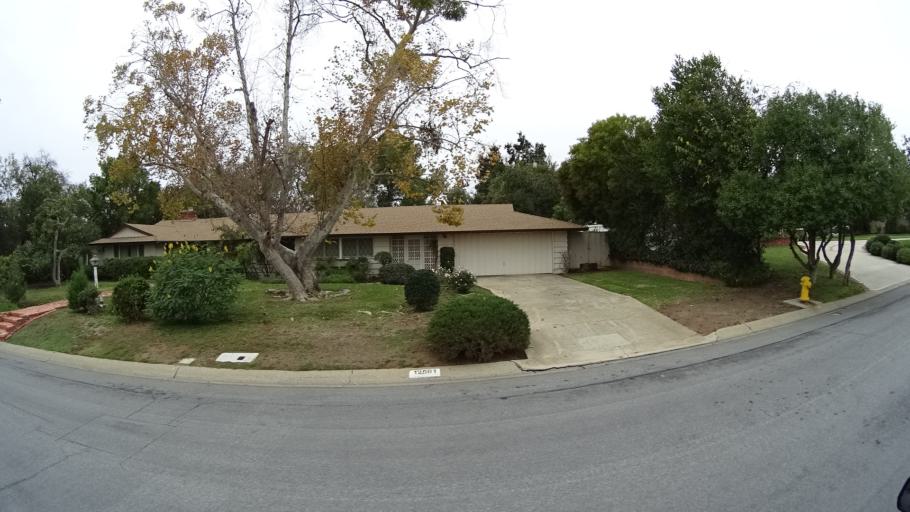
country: US
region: California
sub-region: Orange County
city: North Tustin
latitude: 33.7462
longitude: -117.7949
